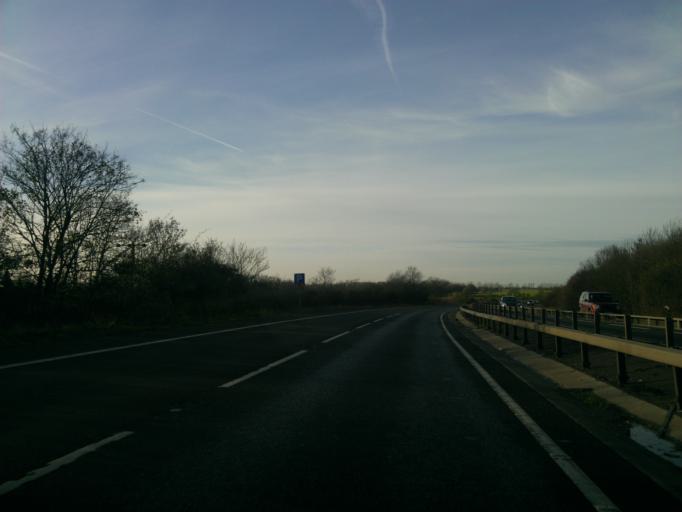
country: GB
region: England
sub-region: Essex
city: Witham
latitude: 51.7875
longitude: 0.6410
